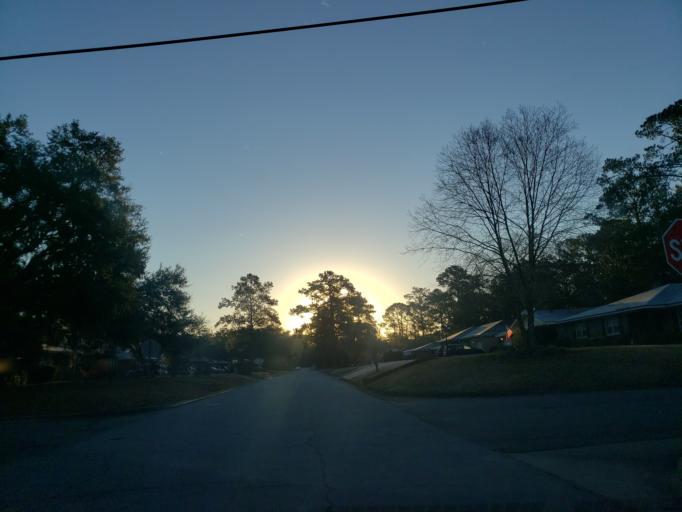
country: US
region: Georgia
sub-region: Chatham County
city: Thunderbolt
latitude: 32.0161
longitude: -81.0805
